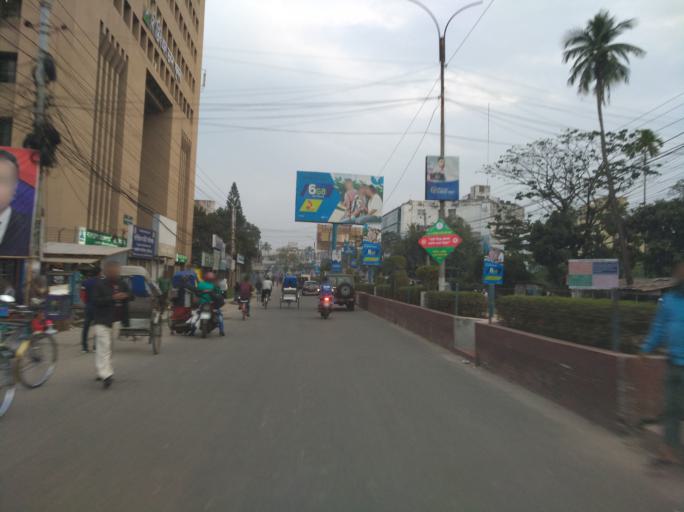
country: BD
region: Khulna
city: Khulna
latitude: 22.8241
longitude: 89.5521
